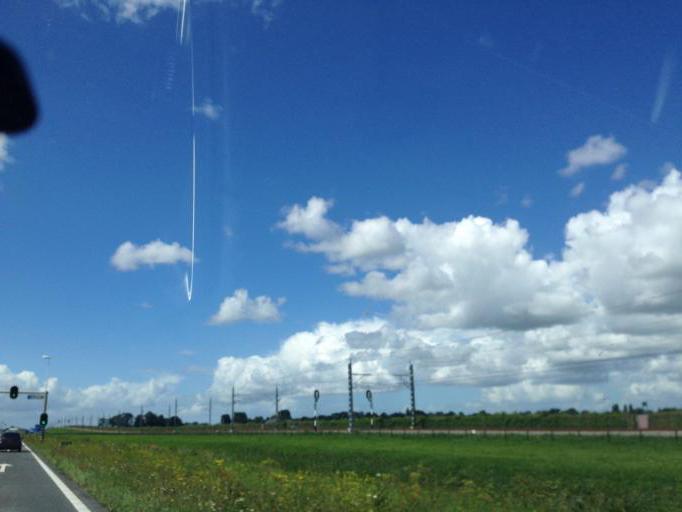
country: NL
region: Overijssel
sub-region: Gemeente Kampen
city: Kampen
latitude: 52.5061
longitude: 5.9715
